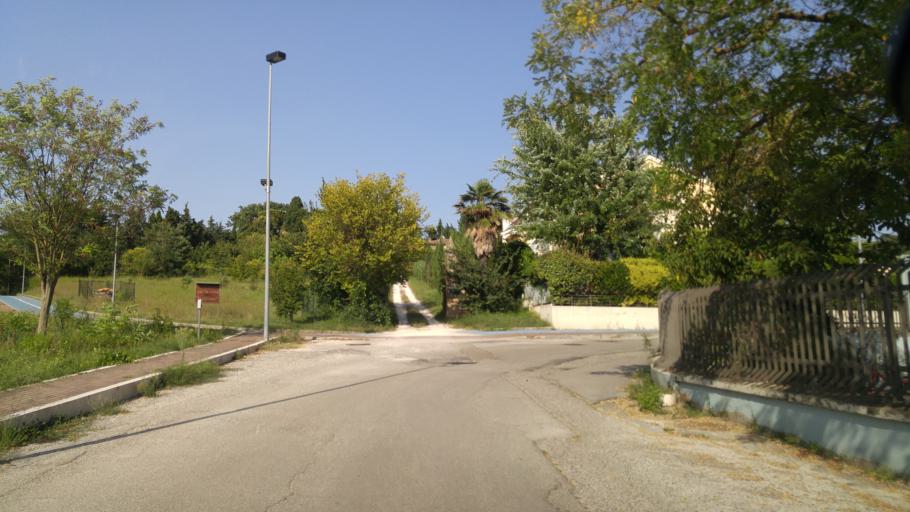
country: IT
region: The Marches
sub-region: Provincia di Pesaro e Urbino
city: Pesaro
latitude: 43.8922
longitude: 12.9250
